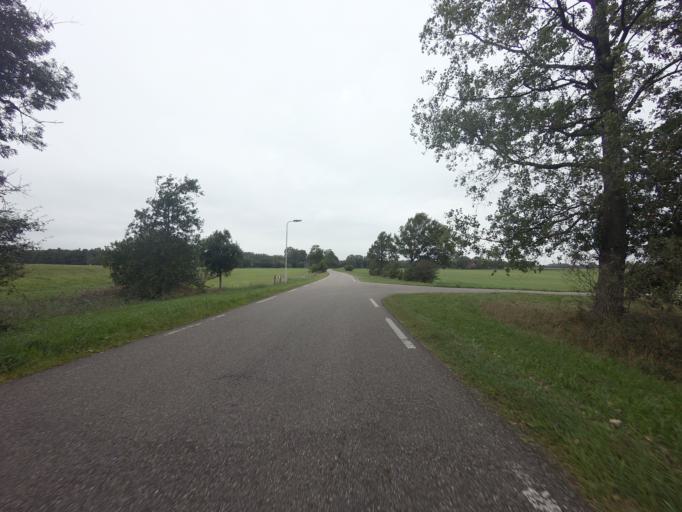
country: NL
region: Friesland
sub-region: Gemeente Opsterland
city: Tijnje
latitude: 53.0231
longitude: 6.0069
